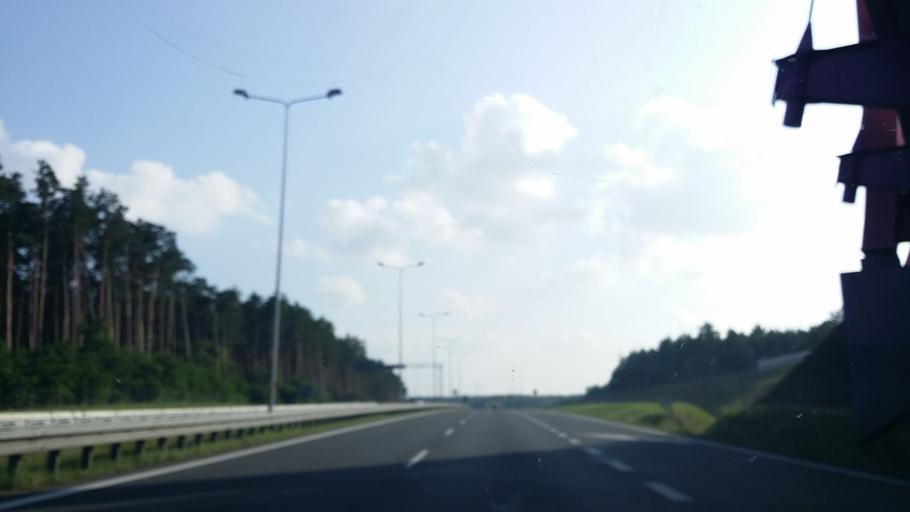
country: PL
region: Lubusz
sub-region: Powiat miedzyrzecki
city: Miedzyrzecz
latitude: 52.4184
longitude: 15.5501
